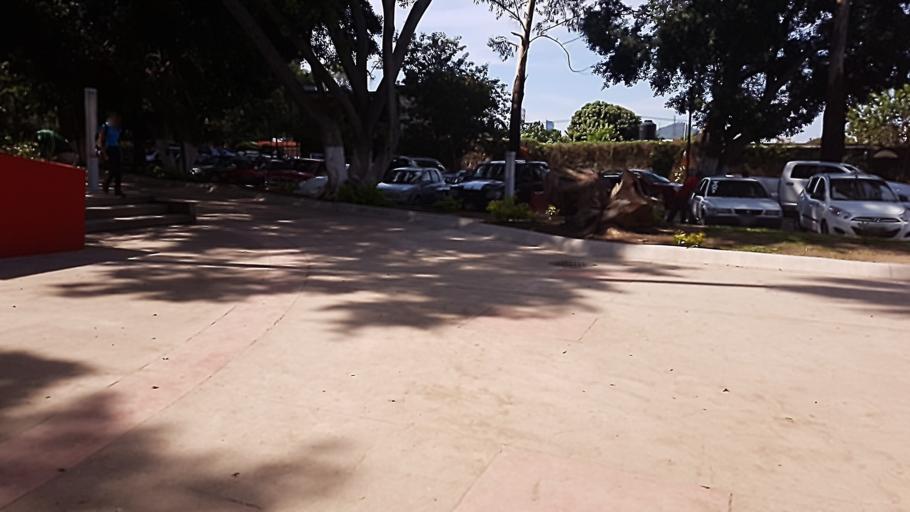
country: MX
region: Nayarit
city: Tepic
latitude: 21.5028
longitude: -104.8967
